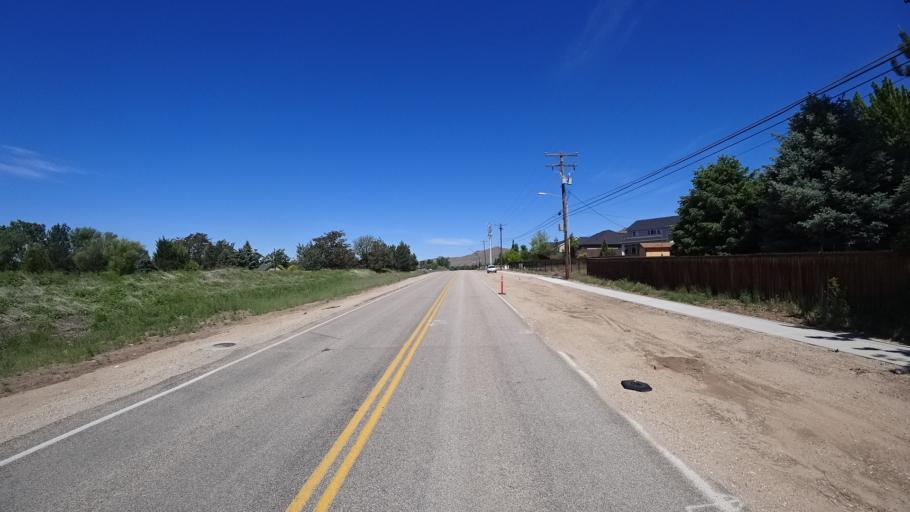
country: US
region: Idaho
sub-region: Ada County
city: Boise
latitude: 43.5597
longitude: -116.1020
